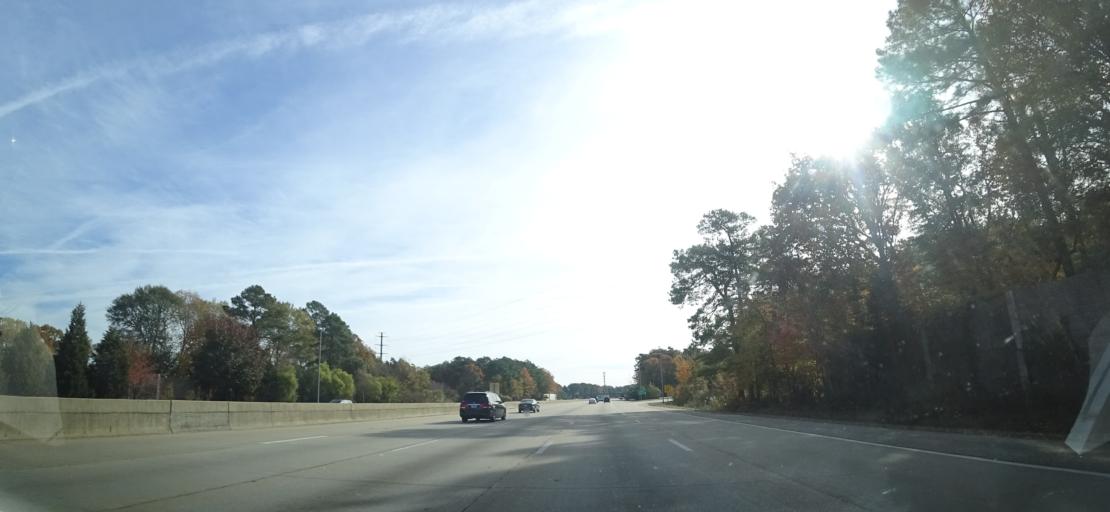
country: US
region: Virginia
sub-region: York County
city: Yorktown
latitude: 37.1114
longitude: -76.4815
